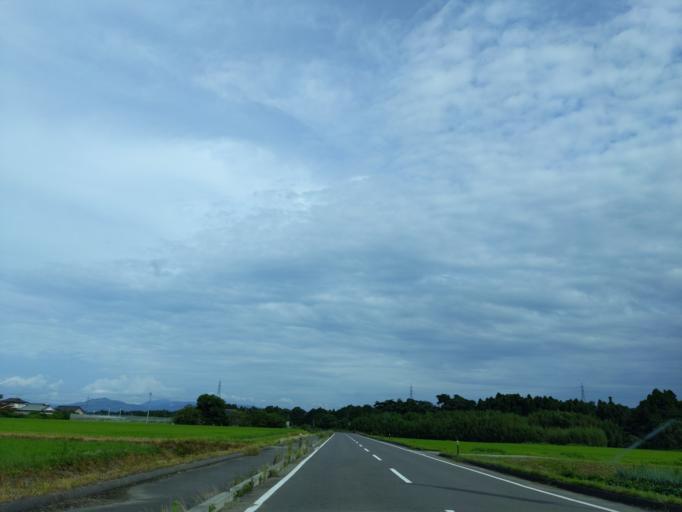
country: JP
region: Fukushima
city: Sukagawa
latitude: 37.3275
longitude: 140.3222
